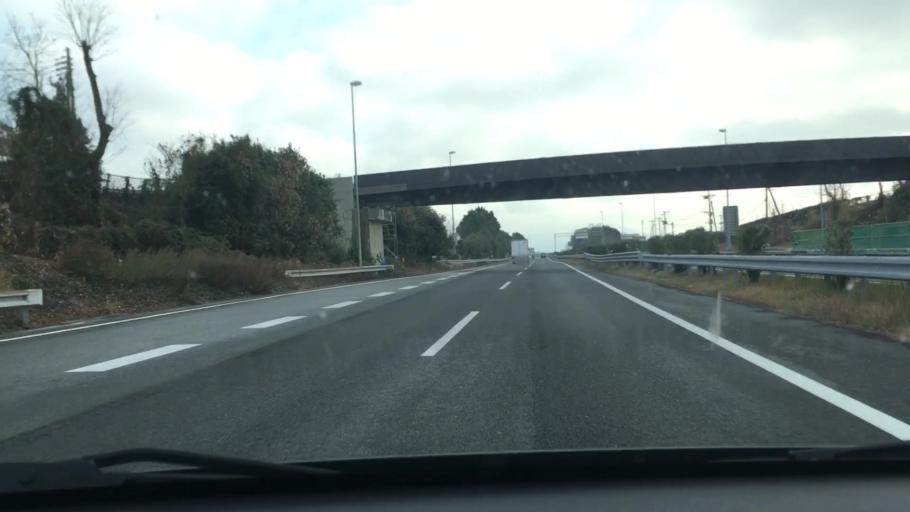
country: JP
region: Kumamoto
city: Kumamoto
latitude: 32.8339
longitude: 130.7799
